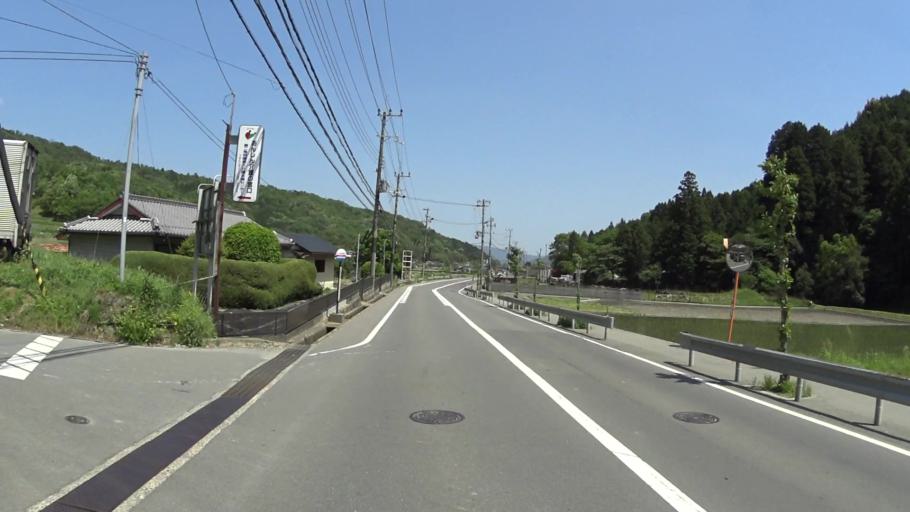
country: JP
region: Kyoto
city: Kameoka
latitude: 35.0262
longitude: 135.5119
